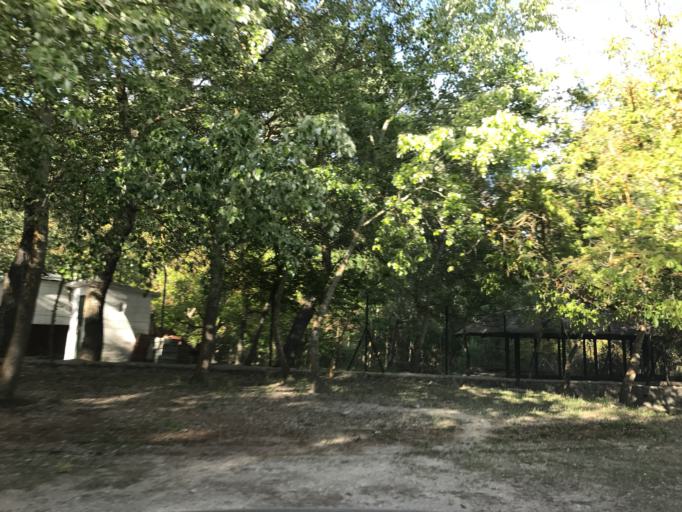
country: ES
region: Andalusia
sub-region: Provincia de Granada
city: Quentar
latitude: 37.2331
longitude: -3.4072
